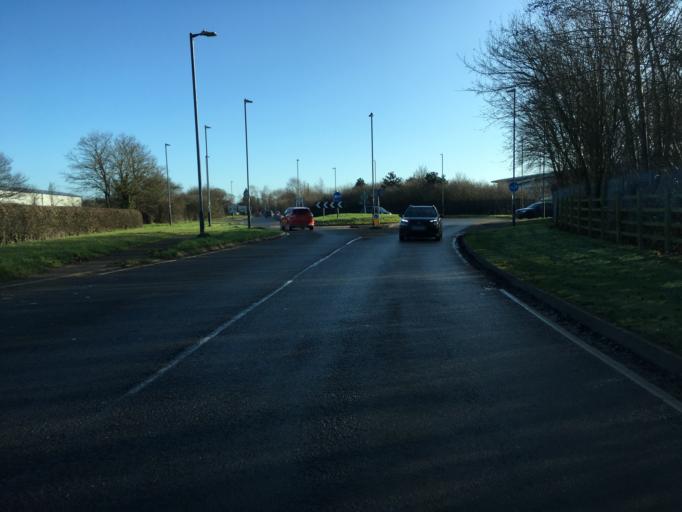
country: GB
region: England
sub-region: Warwickshire
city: Wellesbourne Mountford
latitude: 52.1963
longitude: -1.6061
